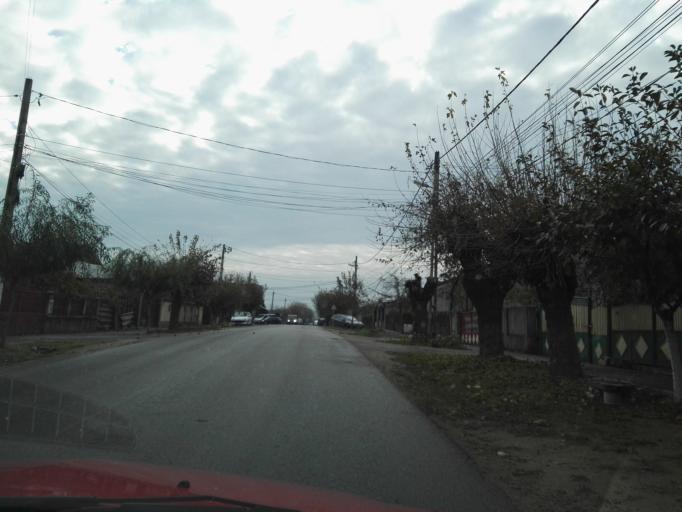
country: RO
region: Ilfov
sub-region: Comuna Magurele
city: Alunisu
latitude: 44.3346
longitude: 26.0641
